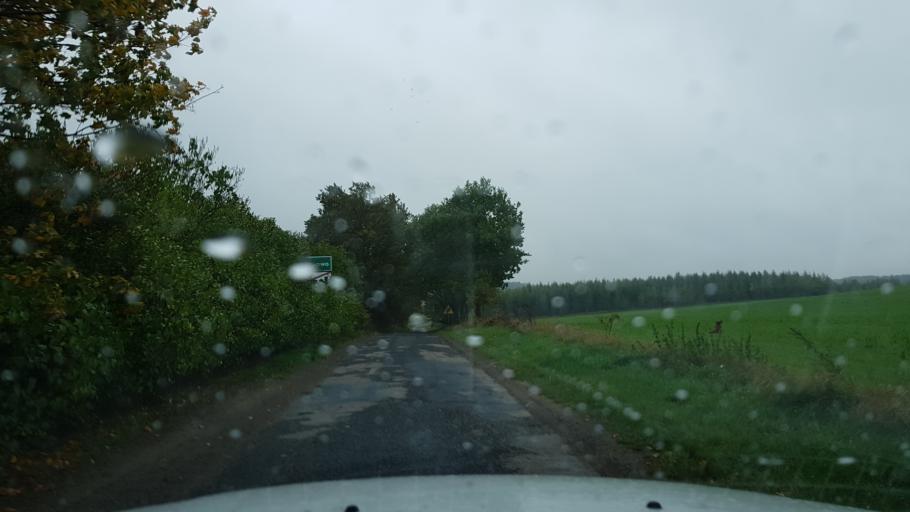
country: PL
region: West Pomeranian Voivodeship
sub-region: Powiat mysliborski
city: Barlinek
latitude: 53.0447
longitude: 15.2396
